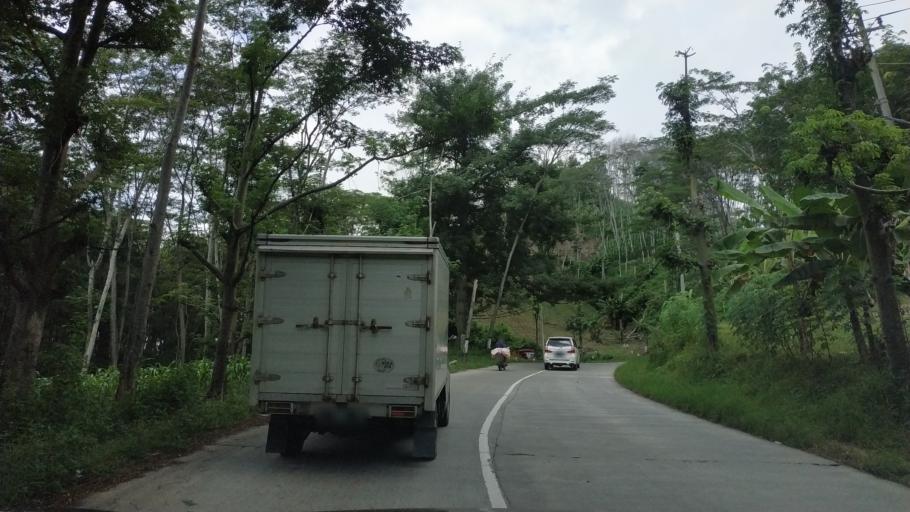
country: ID
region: Central Java
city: Weleri
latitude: -7.0034
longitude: 110.0597
